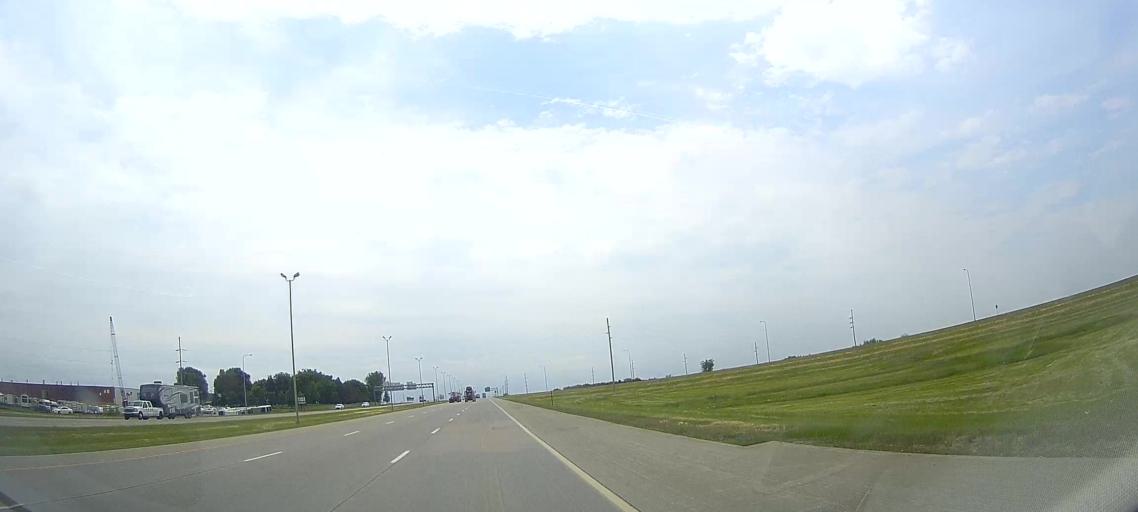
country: US
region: South Dakota
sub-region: Minnehaha County
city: Crooks
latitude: 43.5998
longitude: -96.7714
